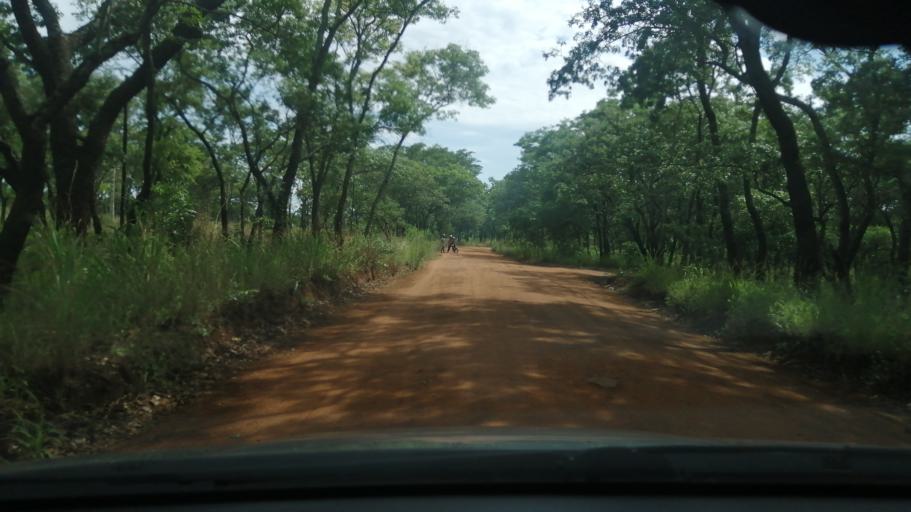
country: ZW
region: Mashonaland West
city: Norton
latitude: -17.8657
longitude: 30.7995
